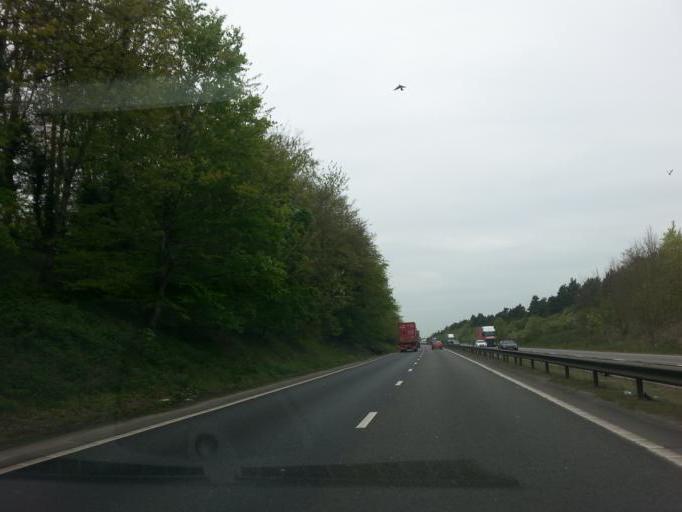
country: GB
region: England
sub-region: Suffolk
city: Bury St Edmunds
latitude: 52.2666
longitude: 0.5608
